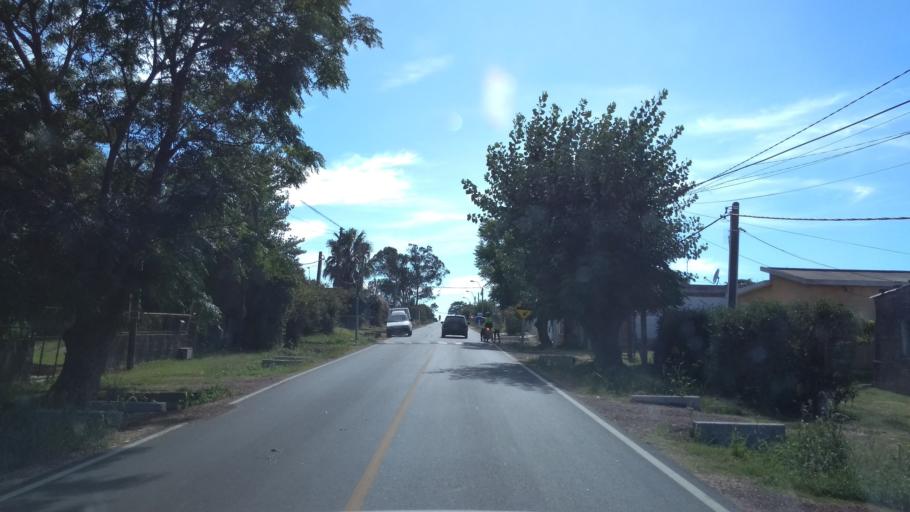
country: UY
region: Canelones
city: Joaquin Suarez
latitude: -34.7308
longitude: -56.0322
